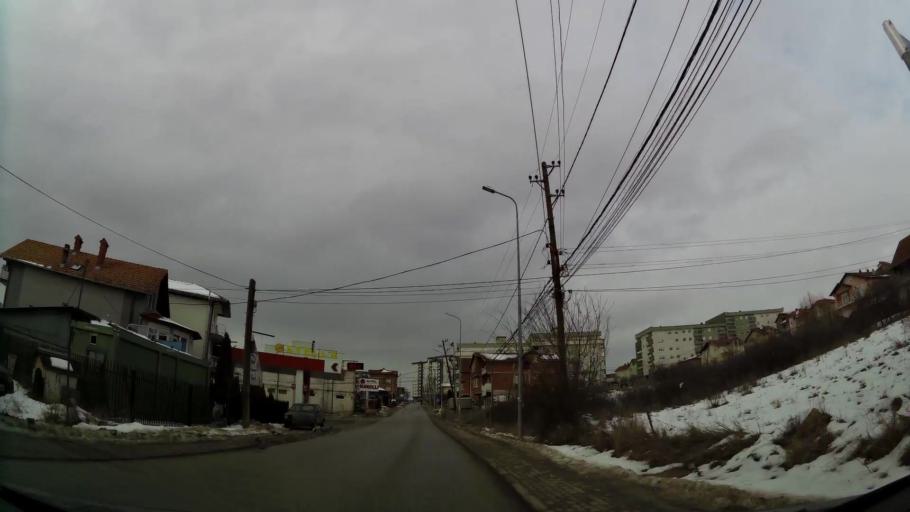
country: XK
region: Pristina
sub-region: Komuna e Prishtines
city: Pristina
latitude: 42.6518
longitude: 21.1930
